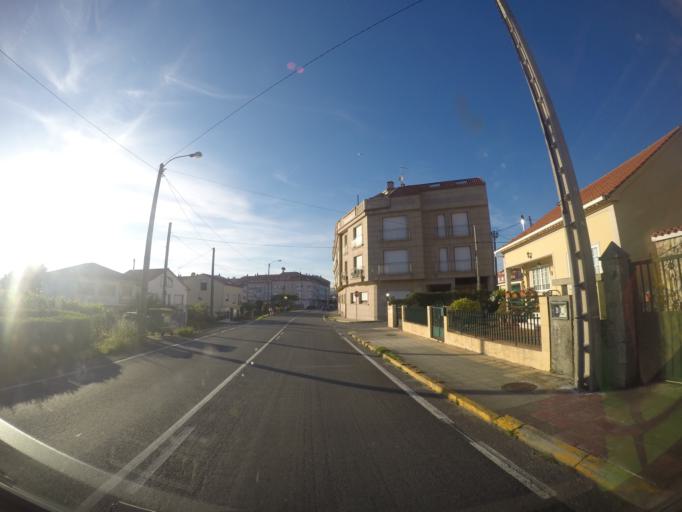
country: ES
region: Galicia
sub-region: Provincia da Coruna
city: Porto do Son
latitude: 42.7539
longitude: -8.9495
